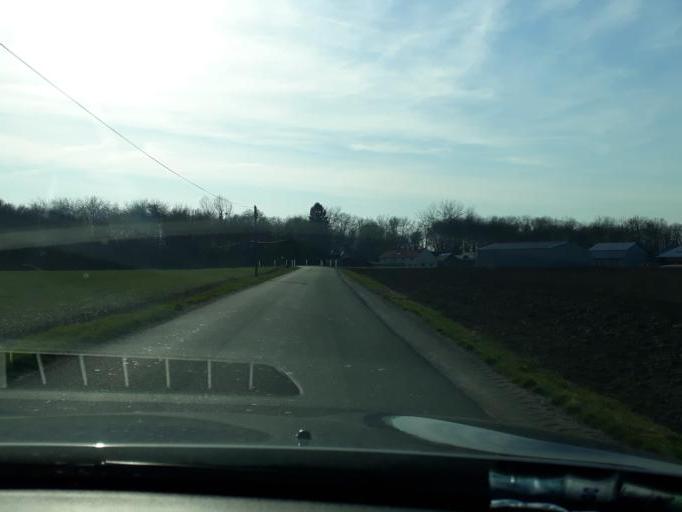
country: FR
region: Centre
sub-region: Departement du Loiret
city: Meung-sur-Loire
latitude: 47.8611
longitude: 1.6853
